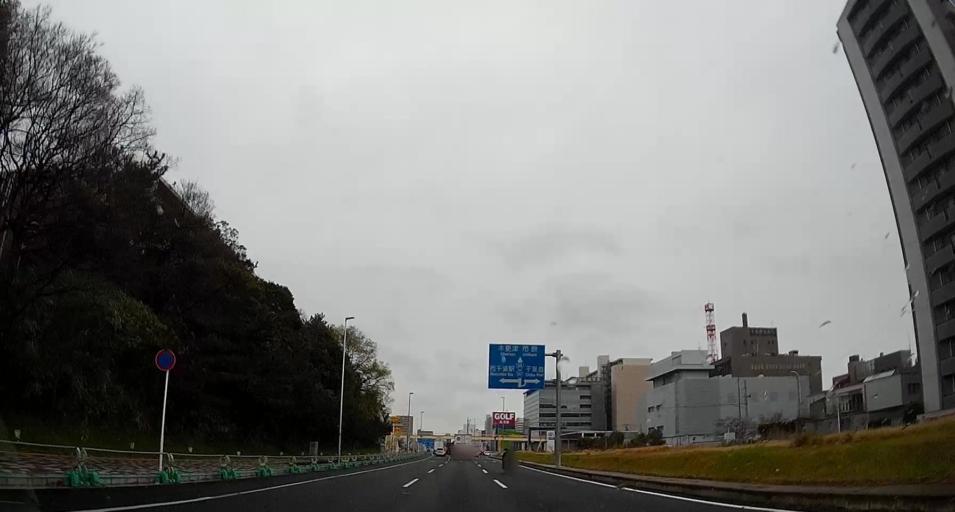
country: JP
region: Chiba
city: Chiba
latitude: 35.6189
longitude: 140.0979
